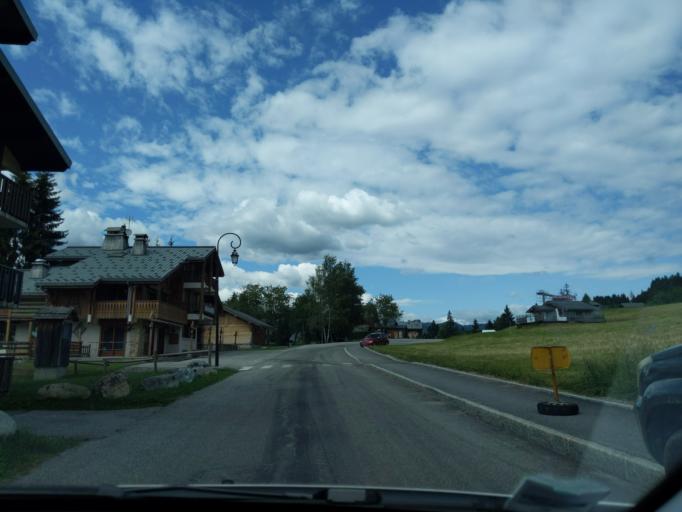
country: FR
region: Rhone-Alpes
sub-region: Departement de la Savoie
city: Ugine
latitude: 45.7837
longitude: 6.4997
